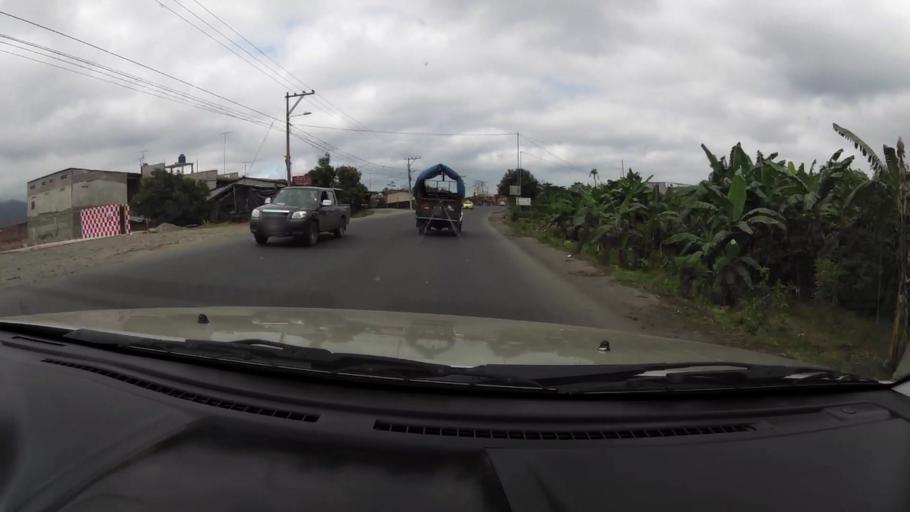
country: EC
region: Guayas
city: Naranjal
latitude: -2.6820
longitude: -79.6214
